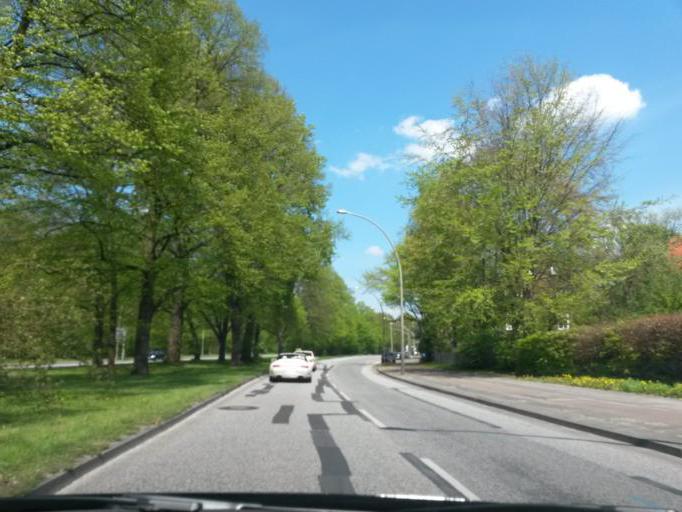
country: DE
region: Hamburg
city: Winterhude
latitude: 53.6040
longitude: 9.9880
